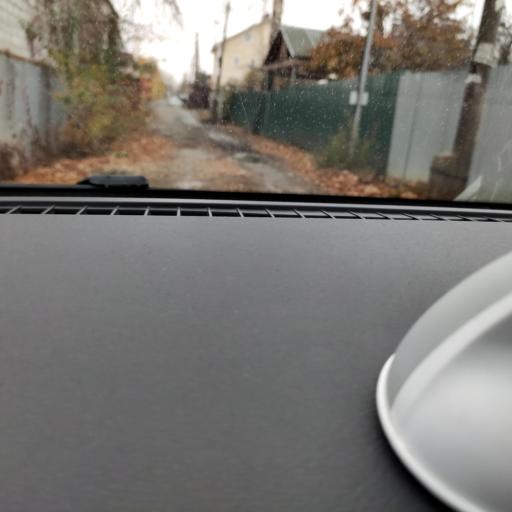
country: RU
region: Samara
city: Samara
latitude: 53.2741
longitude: 50.2108
